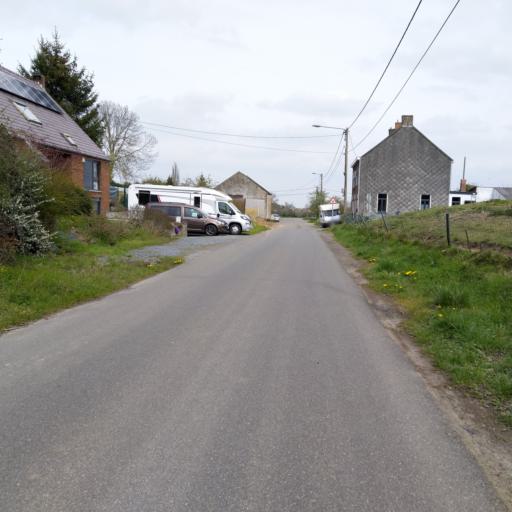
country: FR
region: Nord-Pas-de-Calais
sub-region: Departement du Nord
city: Feignies
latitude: 50.3329
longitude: 3.9027
